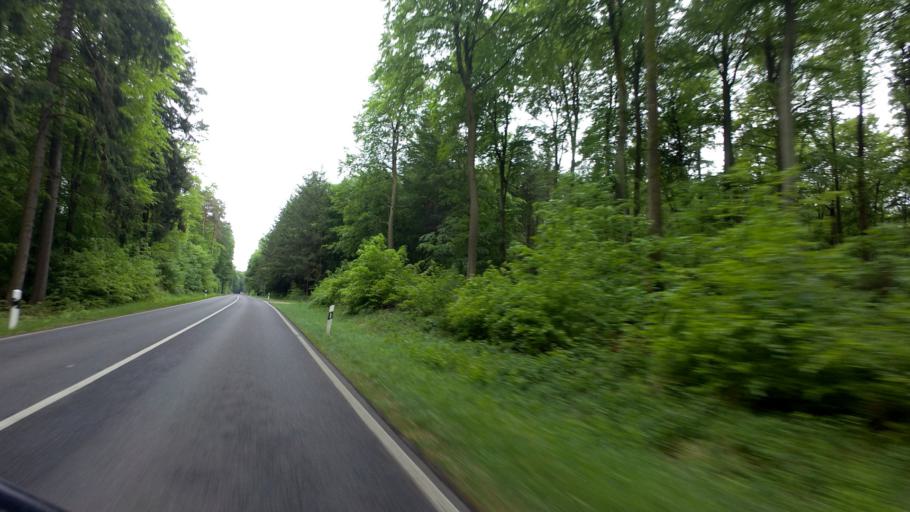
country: DE
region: Brandenburg
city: Lychen
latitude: 53.1870
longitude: 13.3286
